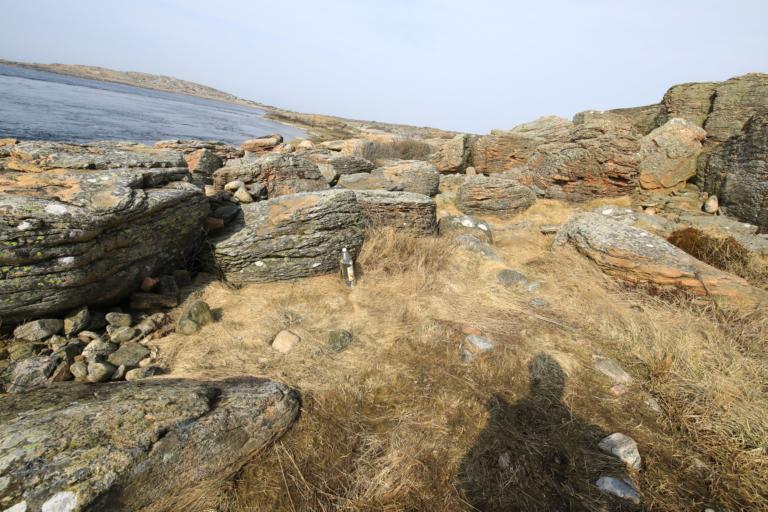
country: SE
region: Halland
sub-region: Kungsbacka Kommun
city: Frillesas
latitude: 57.2515
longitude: 12.0910
